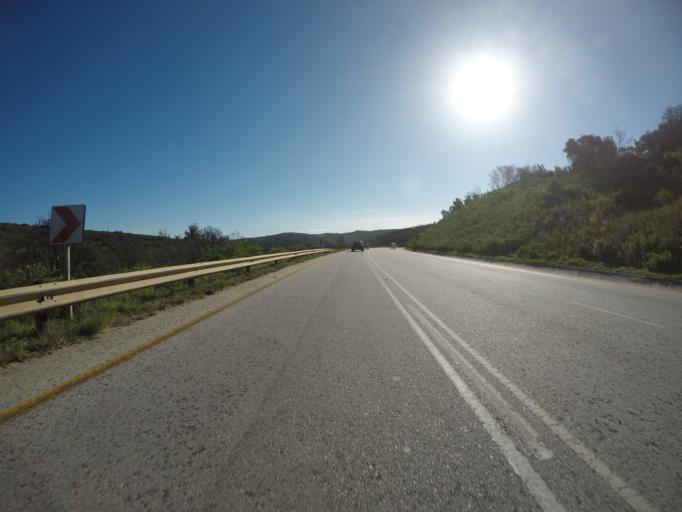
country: ZA
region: Eastern Cape
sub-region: Cacadu District Municipality
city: Jeffrey's Bay
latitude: -33.9032
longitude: 25.1014
